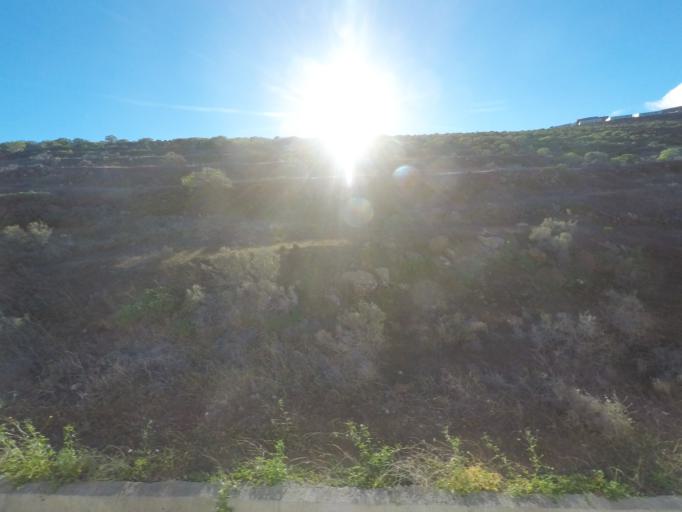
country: ES
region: Canary Islands
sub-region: Provincia de Santa Cruz de Tenerife
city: San Sebastian de la Gomera
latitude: 28.0842
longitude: -17.1368
